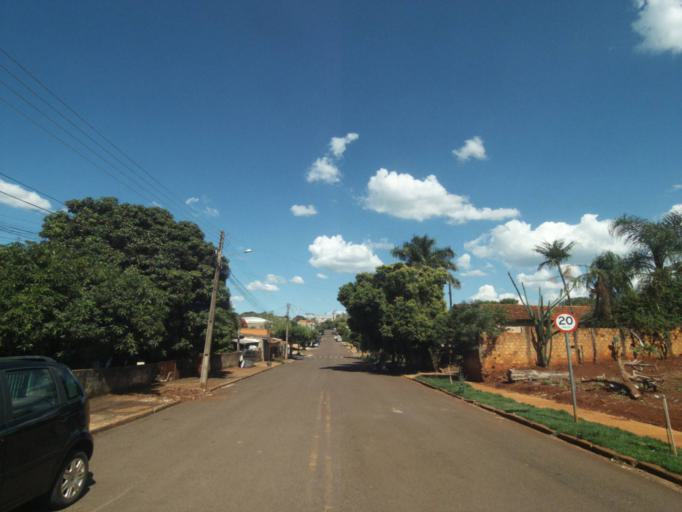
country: BR
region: Parana
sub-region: Sertanopolis
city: Sertanopolis
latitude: -23.0426
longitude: -50.8219
